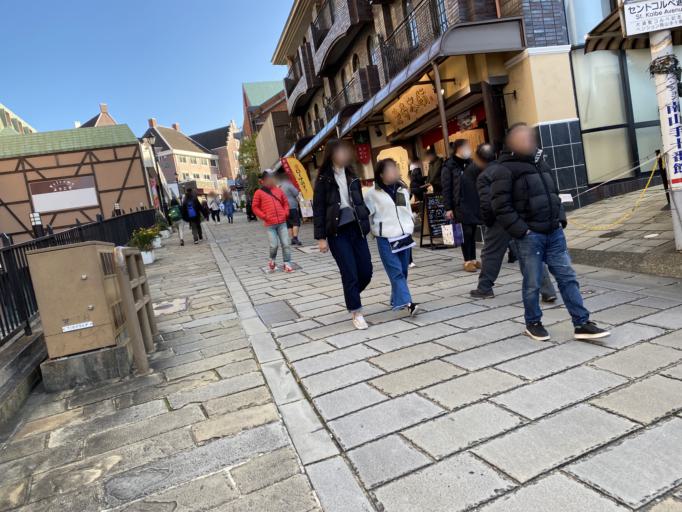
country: JP
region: Nagasaki
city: Nagasaki-shi
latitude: 32.7357
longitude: 129.8699
